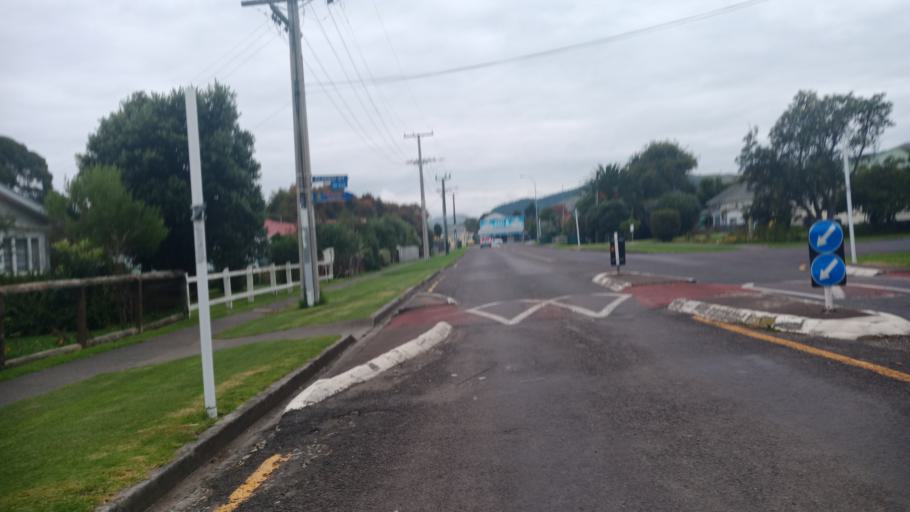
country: NZ
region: Gisborne
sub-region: Gisborne District
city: Gisborne
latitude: -38.6760
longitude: 178.0427
